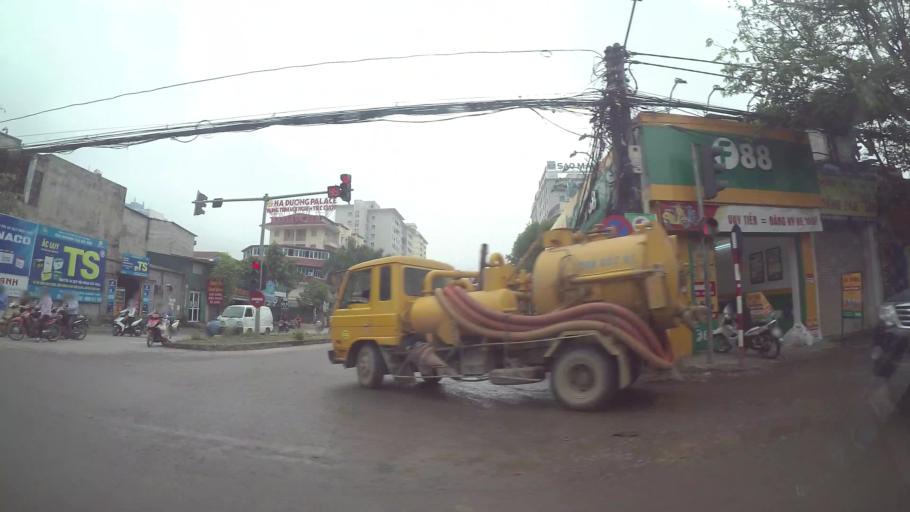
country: VN
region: Ha Noi
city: Hai BaTrung
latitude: 20.9836
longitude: 105.8639
